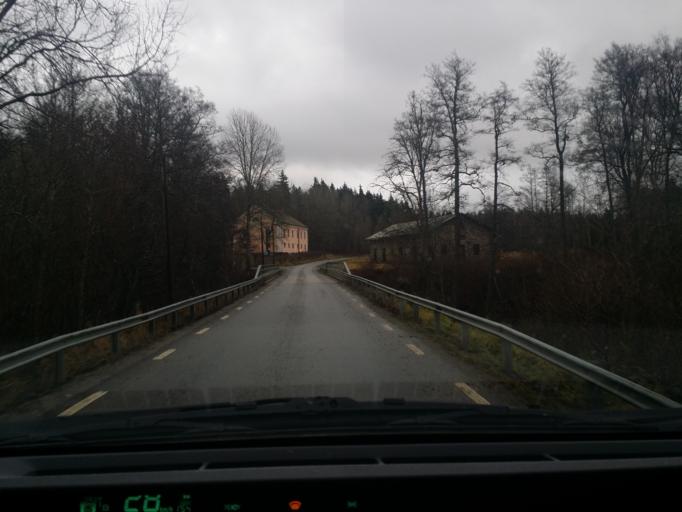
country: SE
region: Vaestmanland
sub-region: Vasteras
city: Skultuna
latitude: 59.7830
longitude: 16.3822
